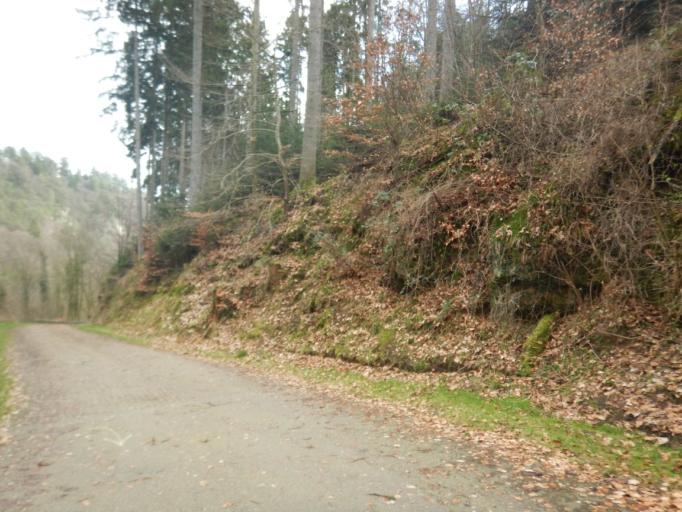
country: LU
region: Luxembourg
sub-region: Canton de Mersch
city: Tuntange
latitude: 49.7109
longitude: 6.0568
